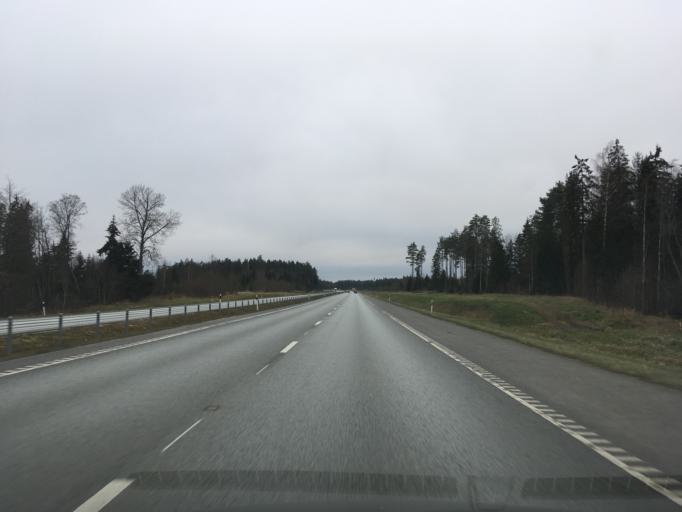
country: EE
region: Laeaene-Virumaa
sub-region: Kadrina vald
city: Kadrina
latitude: 59.4567
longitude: 26.0447
